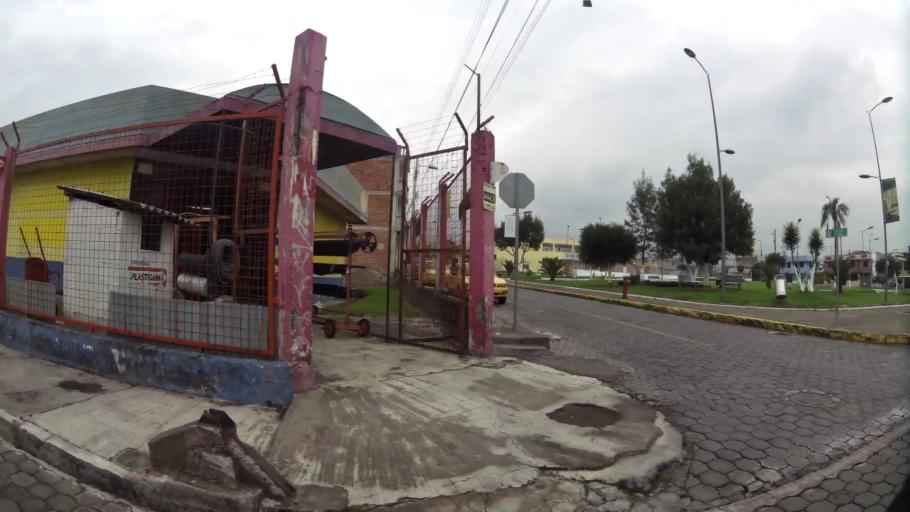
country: EC
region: Pichincha
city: Sangolqui
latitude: -0.3259
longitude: -78.4621
